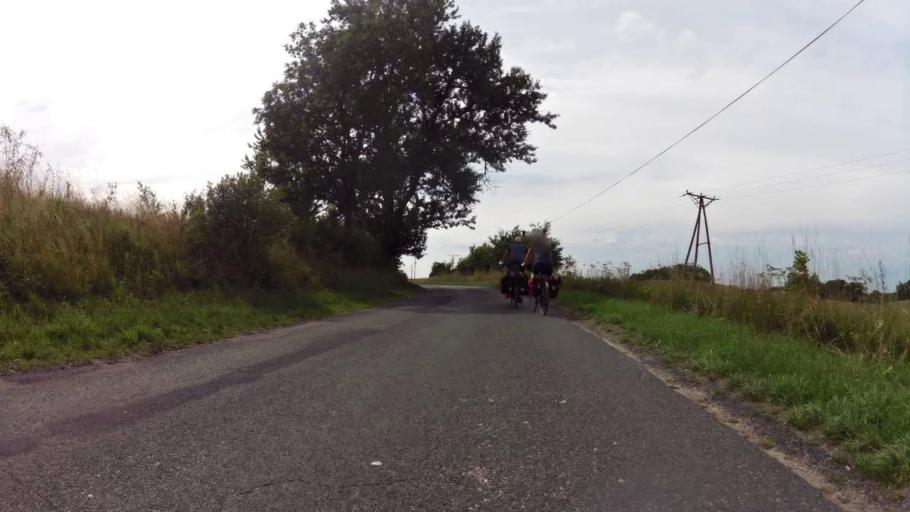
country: PL
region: West Pomeranian Voivodeship
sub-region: Powiat lobeski
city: Wegorzyno
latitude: 53.5424
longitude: 15.5974
